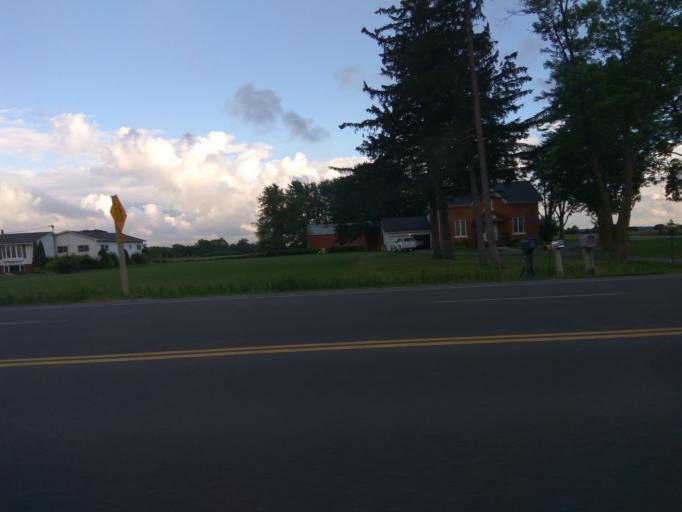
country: CA
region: Ontario
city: Stratford
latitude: 43.3703
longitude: -80.9121
